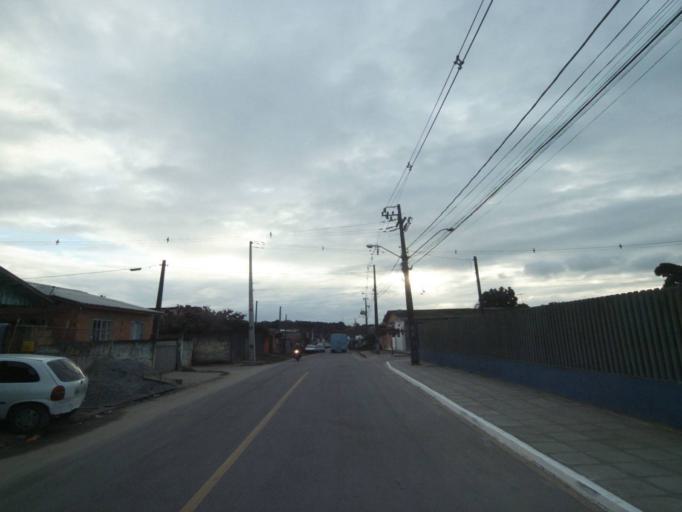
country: BR
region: Parana
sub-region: Paranagua
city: Paranagua
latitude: -25.5311
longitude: -48.5459
